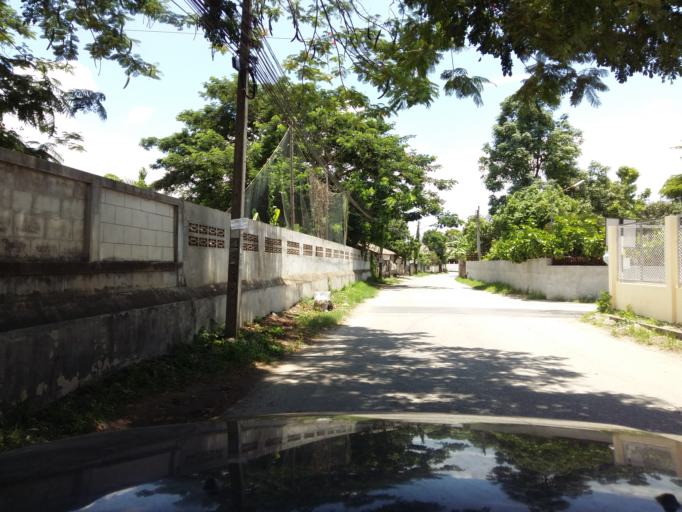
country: TH
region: Chiang Mai
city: Chiang Mai
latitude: 18.7677
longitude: 99.0127
